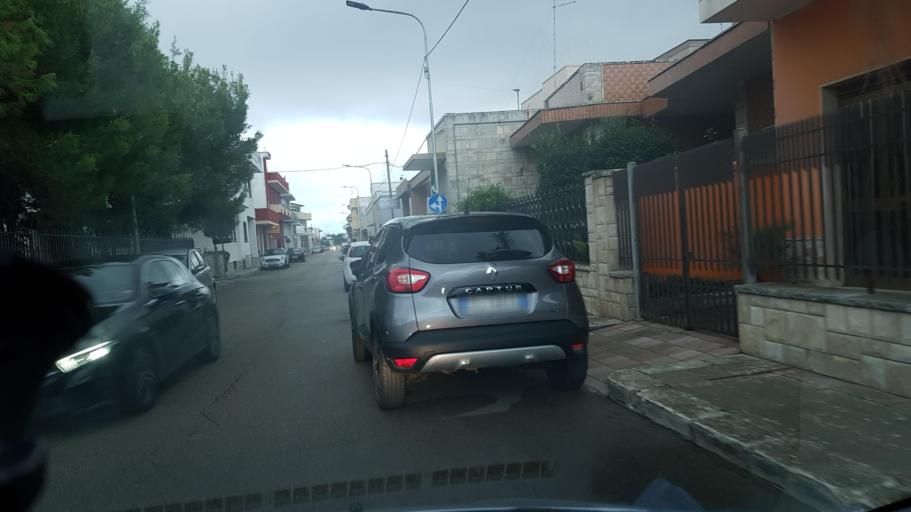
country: IT
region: Apulia
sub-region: Provincia di Lecce
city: Carmiano
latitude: 40.3479
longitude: 18.0376
